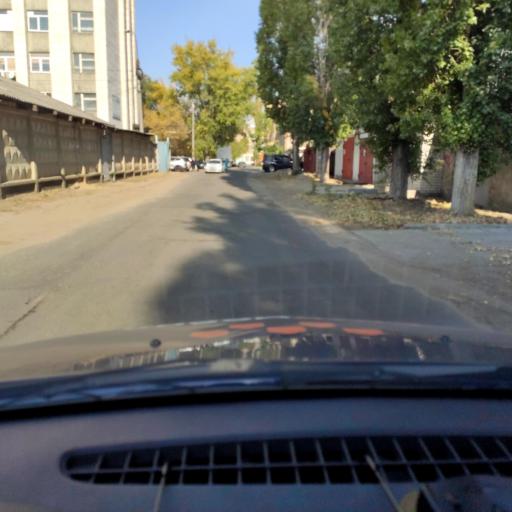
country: RU
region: Voronezj
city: Voronezh
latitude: 51.6330
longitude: 39.2417
